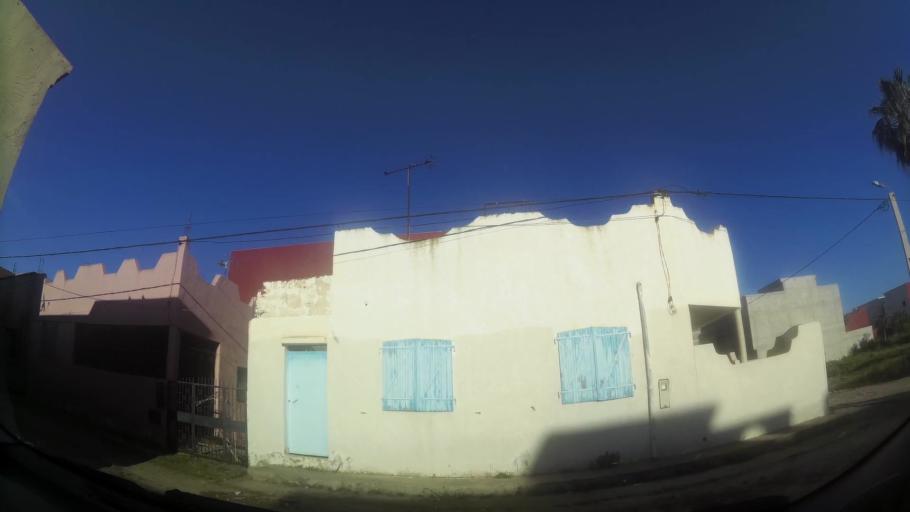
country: MA
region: Oriental
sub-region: Berkane-Taourirt
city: Madagh
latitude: 35.0848
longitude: -2.2486
